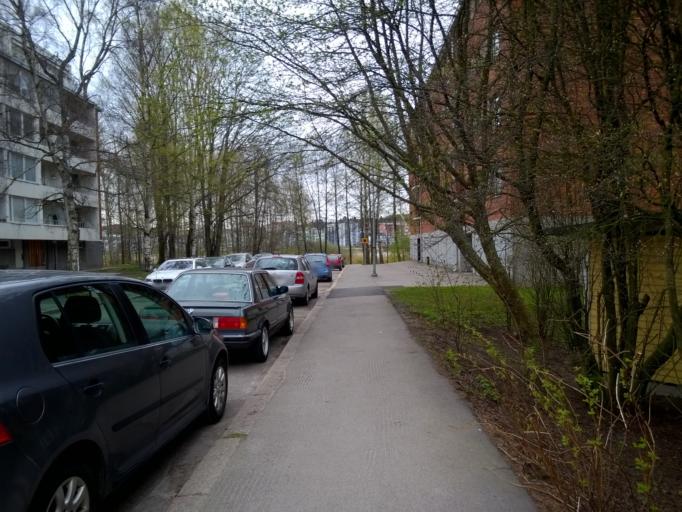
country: FI
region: Uusimaa
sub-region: Helsinki
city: Teekkarikylae
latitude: 60.1983
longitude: 24.8858
